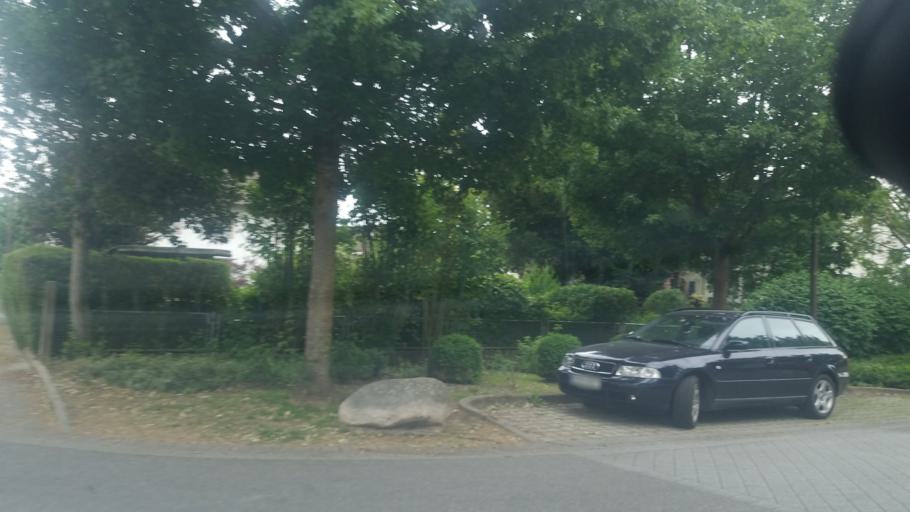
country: DE
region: Baden-Wuerttemberg
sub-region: Freiburg Region
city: Achern
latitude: 48.6182
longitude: 8.0801
